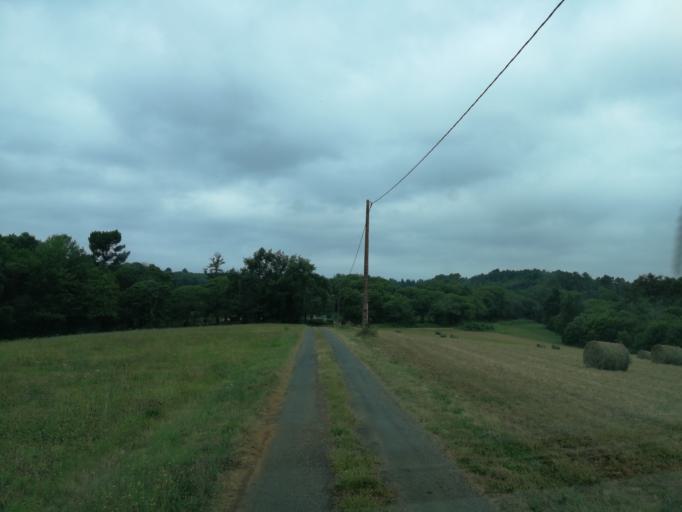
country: FR
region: Midi-Pyrenees
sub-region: Departement du Lot
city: Prayssac
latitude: 44.5684
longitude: 1.0771
